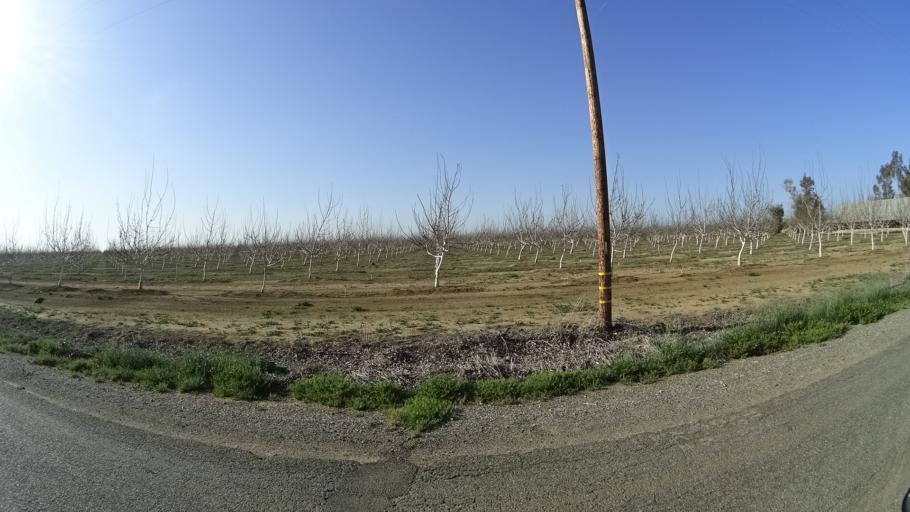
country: US
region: California
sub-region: Glenn County
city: Willows
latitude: 39.5096
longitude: -122.2464
